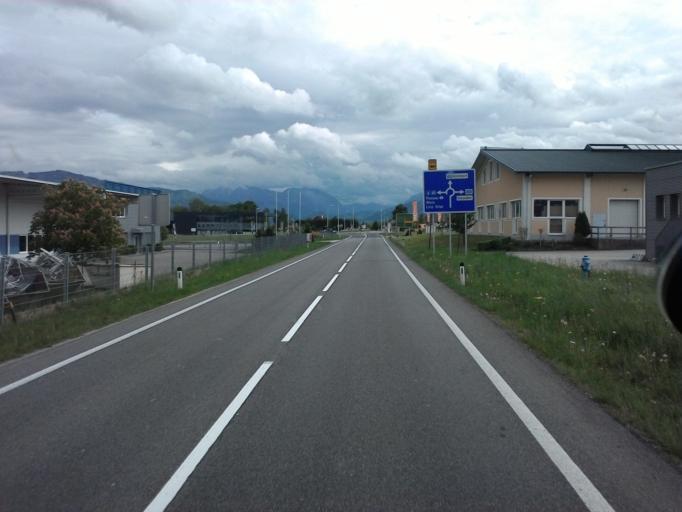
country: AT
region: Upper Austria
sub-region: Politischer Bezirk Kirchdorf an der Krems
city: Micheldorf in Oberoesterreich
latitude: 47.9311
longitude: 14.0857
